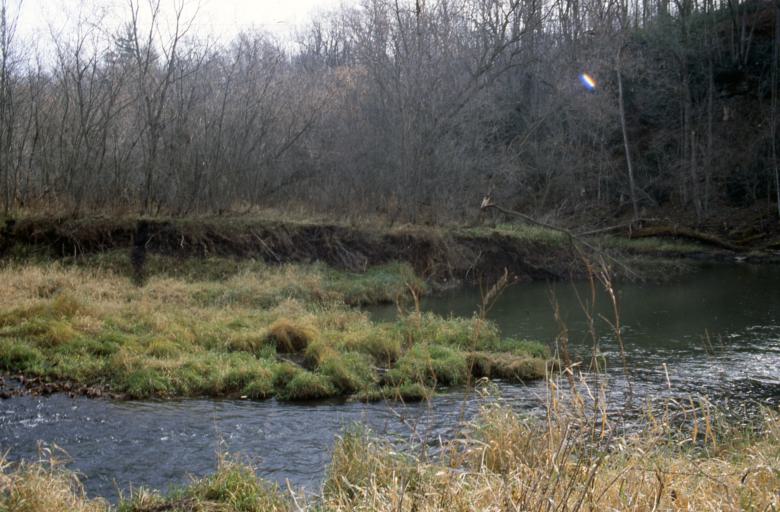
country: US
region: Minnesota
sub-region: Wabasha County
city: Plainview
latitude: 44.1081
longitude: -92.1696
